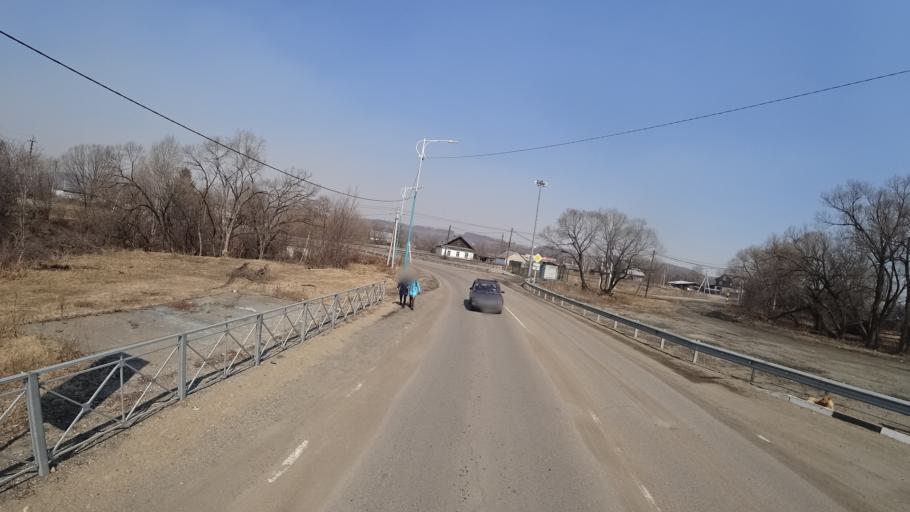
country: RU
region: Amur
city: Novobureyskiy
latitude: 49.7932
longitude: 129.9058
